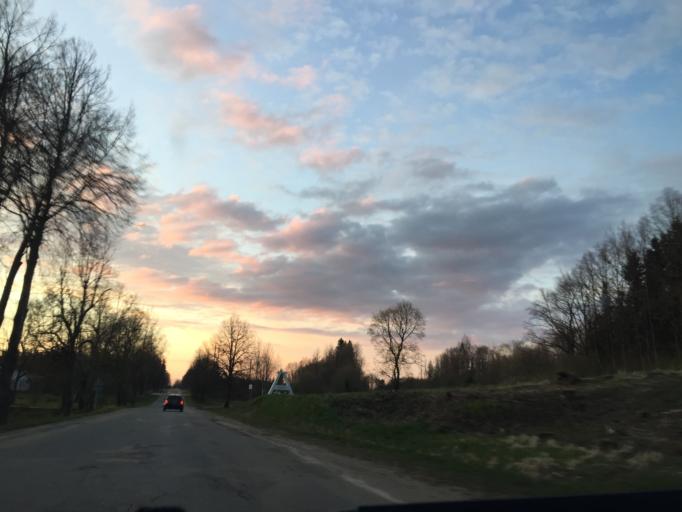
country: LV
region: Aluksnes Rajons
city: Aluksne
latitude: 57.4025
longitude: 27.0468
